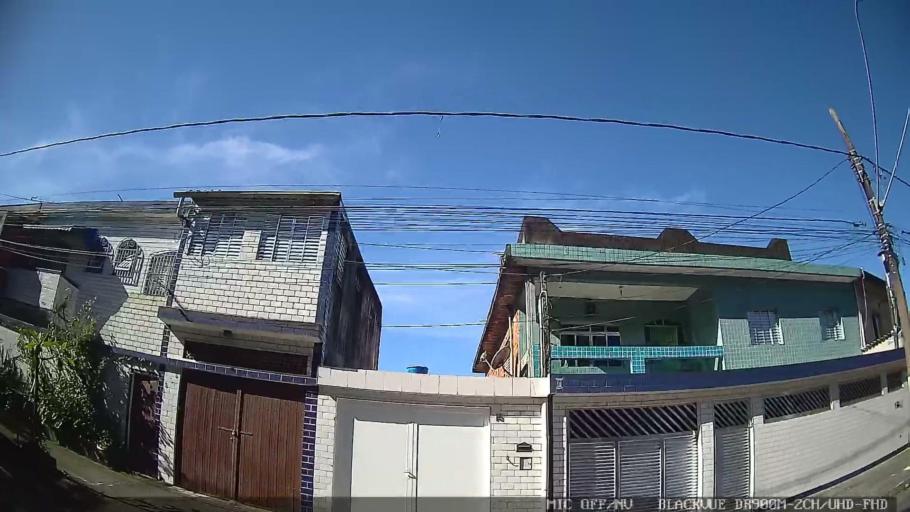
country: BR
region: Sao Paulo
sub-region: Santos
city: Santos
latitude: -23.9338
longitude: -46.2898
